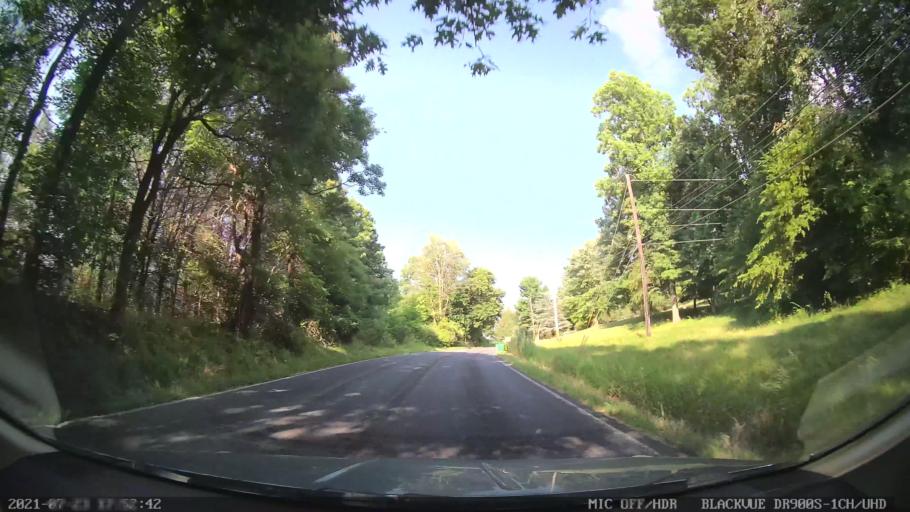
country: US
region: Pennsylvania
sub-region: Lehigh County
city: Macungie
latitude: 40.5032
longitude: -75.5743
